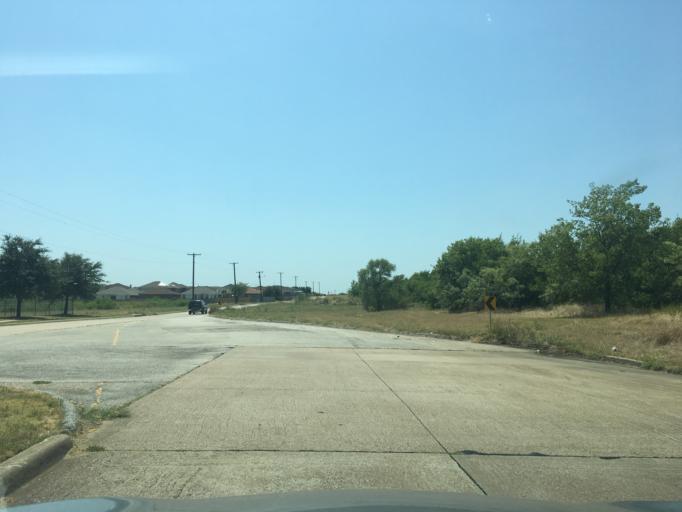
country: US
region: Texas
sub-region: Tarrant County
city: Crowley
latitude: 32.6137
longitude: -97.3721
